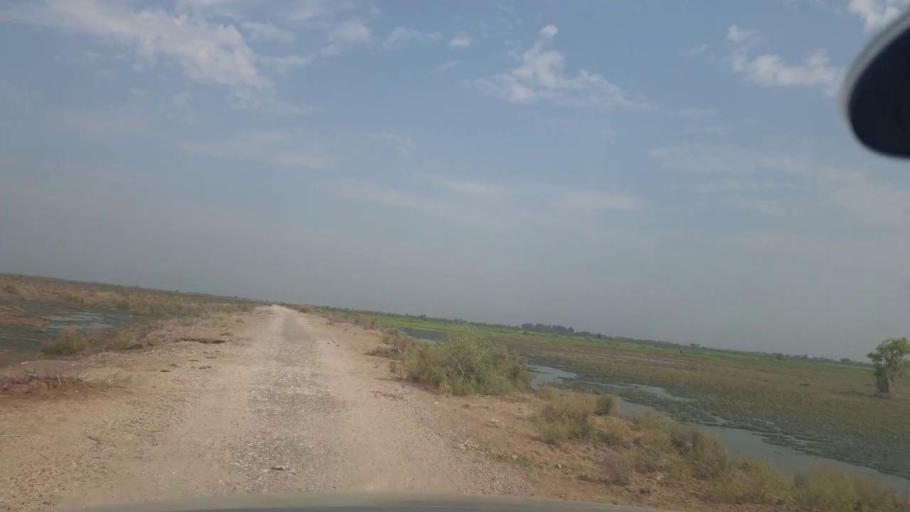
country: PK
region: Balochistan
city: Mehrabpur
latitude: 28.0377
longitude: 68.1258
